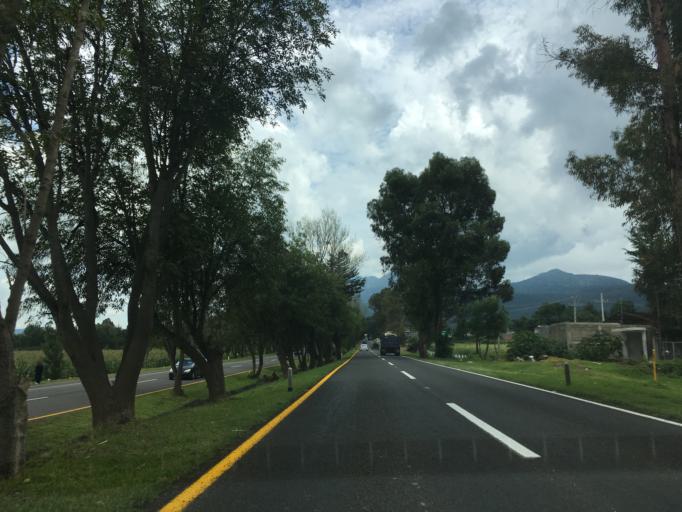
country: MX
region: Michoacan
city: Patzcuaro
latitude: 19.5399
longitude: -101.5785
